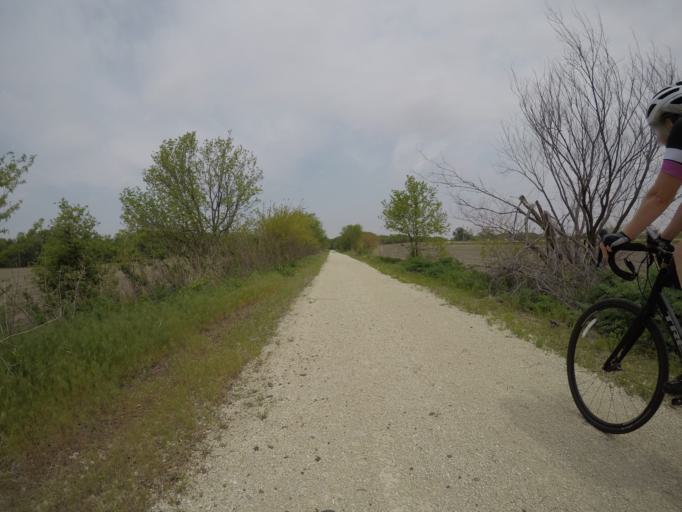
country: US
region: Nebraska
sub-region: Gage County
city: Beatrice
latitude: 40.2453
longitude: -96.6899
